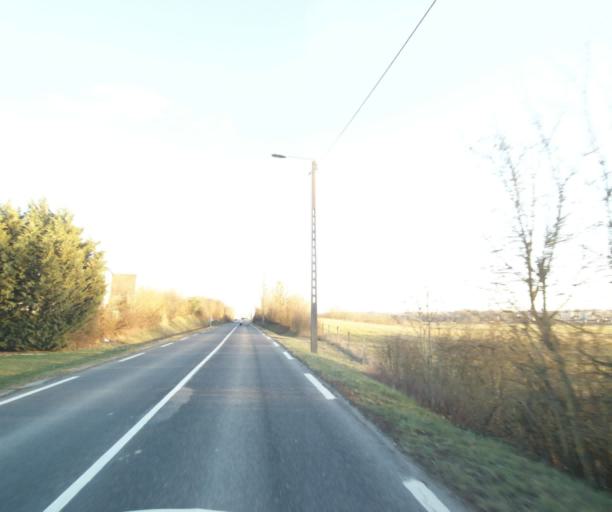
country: FR
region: Lorraine
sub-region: Departement de Meurthe-et-Moselle
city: Laneuveville-devant-Nancy
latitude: 48.6673
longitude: 6.2338
